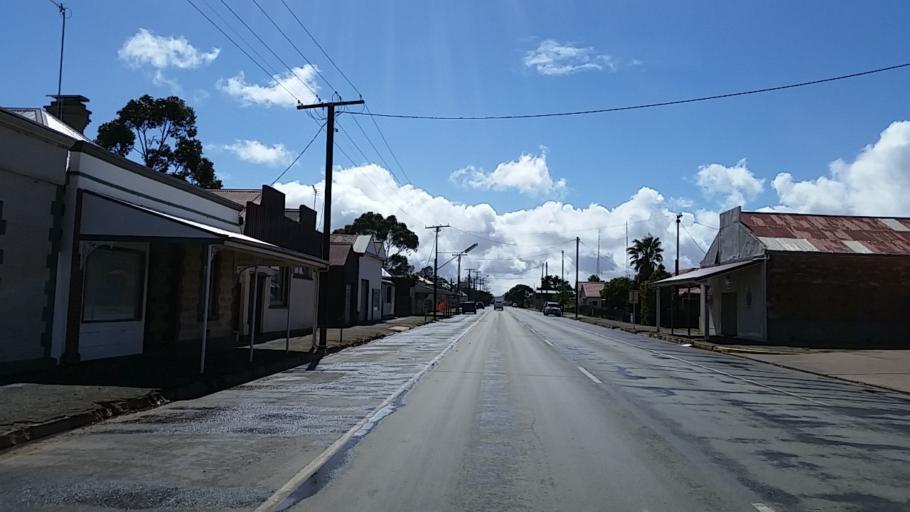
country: AU
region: South Australia
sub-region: Peterborough
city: Peterborough
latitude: -32.9730
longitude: 138.8410
